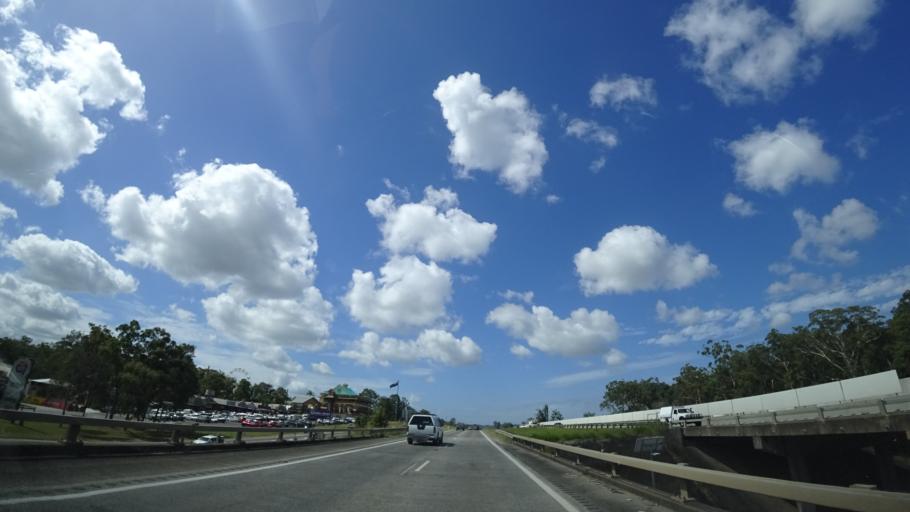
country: AU
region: Queensland
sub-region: Sunshine Coast
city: Little Mountain
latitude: -26.7524
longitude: 153.0470
